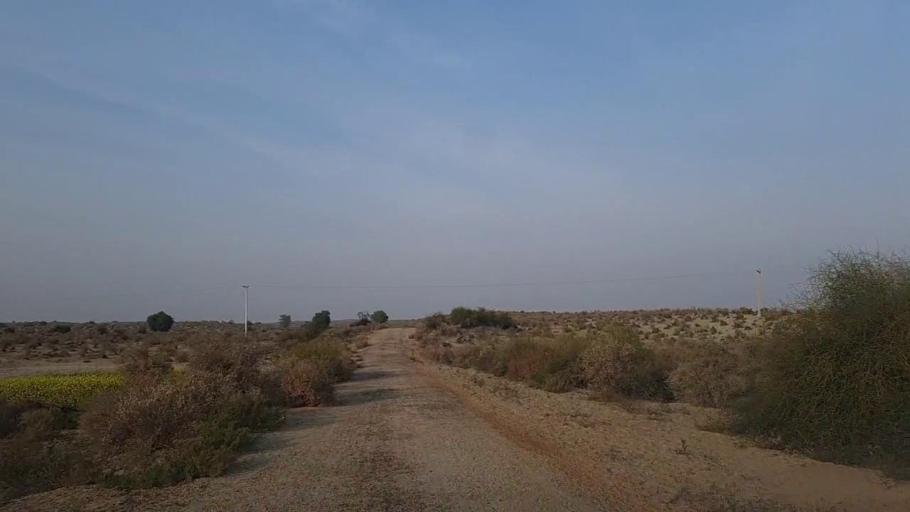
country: PK
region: Sindh
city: Jam Sahib
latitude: 26.4242
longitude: 68.6031
